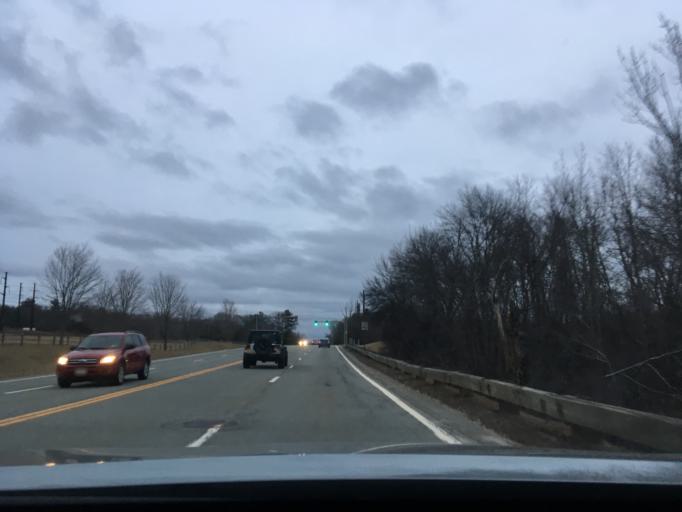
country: US
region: Rhode Island
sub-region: Providence County
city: Smithfield
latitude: 41.9232
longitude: -71.5288
